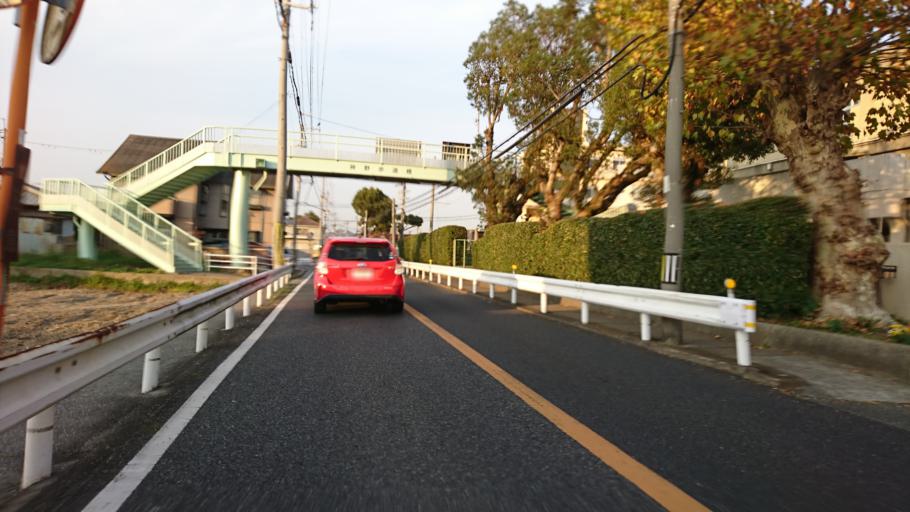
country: JP
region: Hyogo
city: Kakogawacho-honmachi
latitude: 34.7764
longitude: 134.8767
